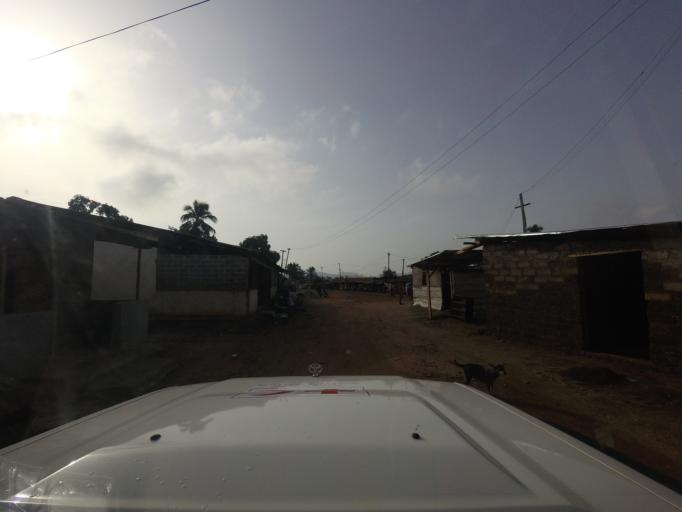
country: LR
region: Lofa
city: Voinjama
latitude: 8.4262
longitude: -9.7570
